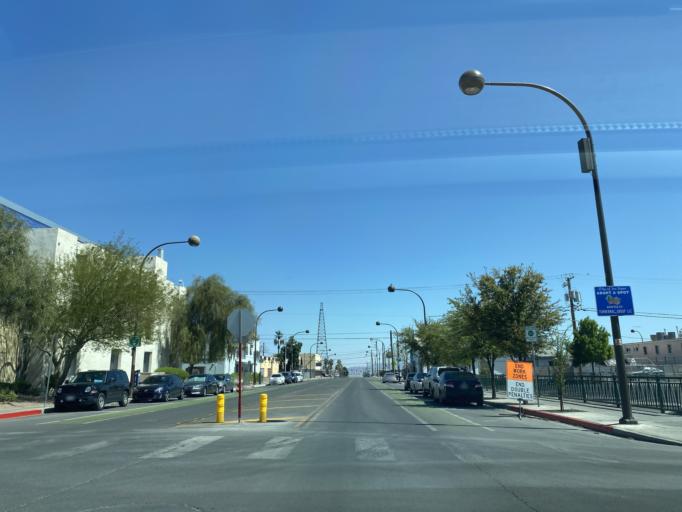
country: US
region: Nevada
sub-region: Clark County
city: Las Vegas
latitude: 36.1690
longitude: -115.1366
